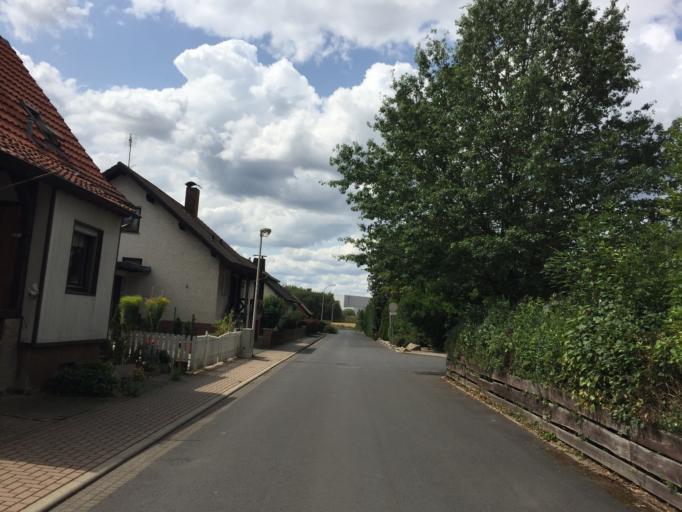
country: DE
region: Hesse
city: Schwalmstadt
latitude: 50.9177
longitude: 9.2318
